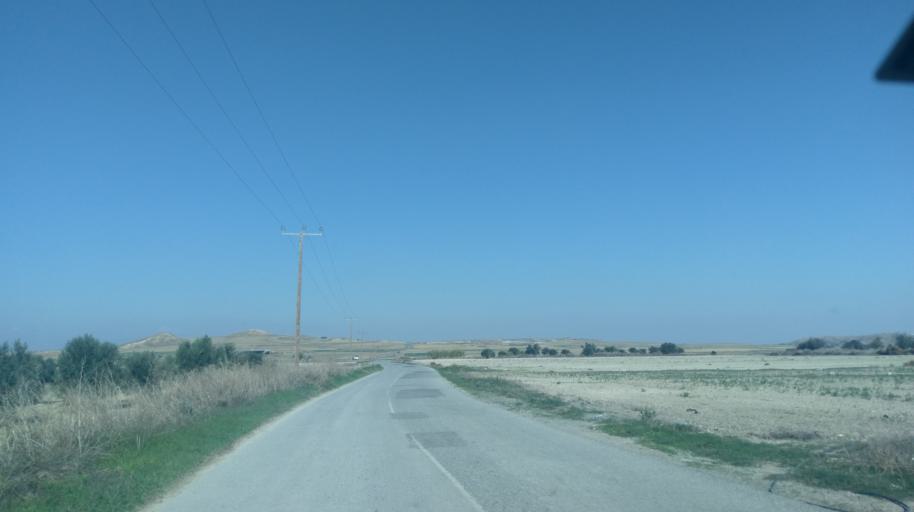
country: CY
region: Lefkosia
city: Lympia
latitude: 35.0325
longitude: 33.4745
